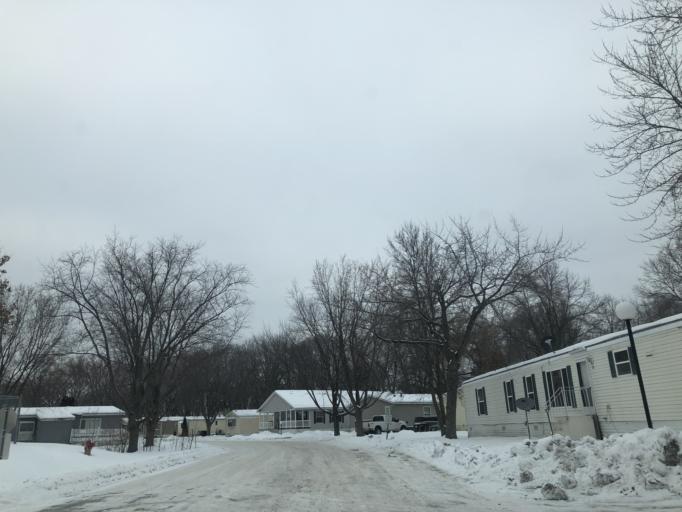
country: US
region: Minnesota
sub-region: Ramsey County
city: New Brighton
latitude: 45.0804
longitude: -93.1805
